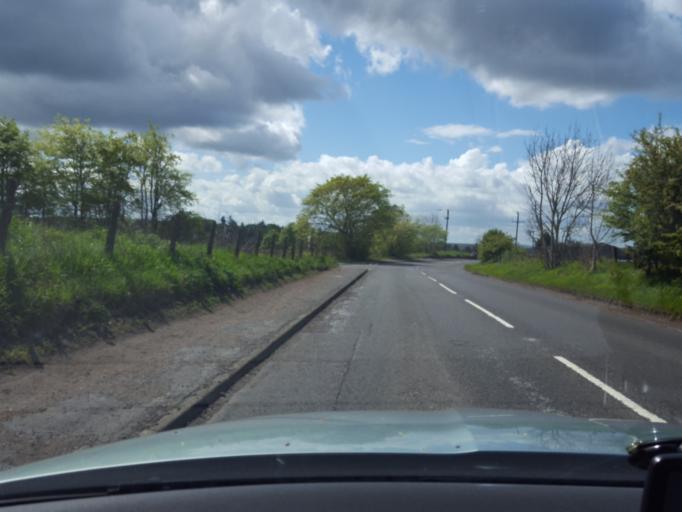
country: GB
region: Scotland
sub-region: Angus
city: Brechin
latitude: 56.7446
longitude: -2.6498
